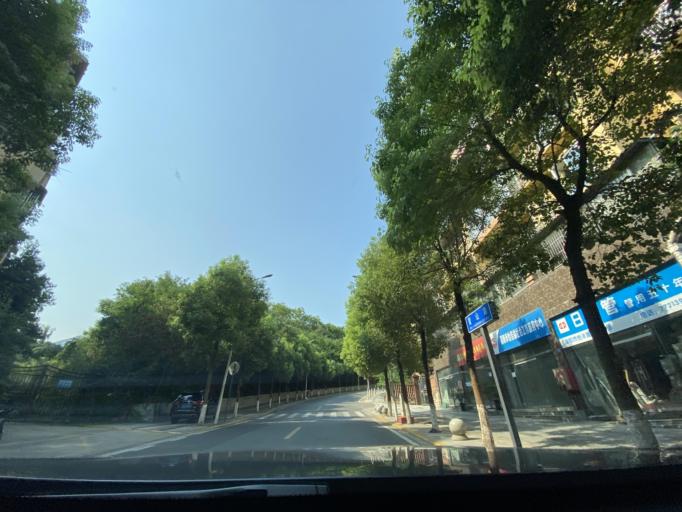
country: CN
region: Sichuan
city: Jiancheng
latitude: 30.4182
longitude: 104.5441
